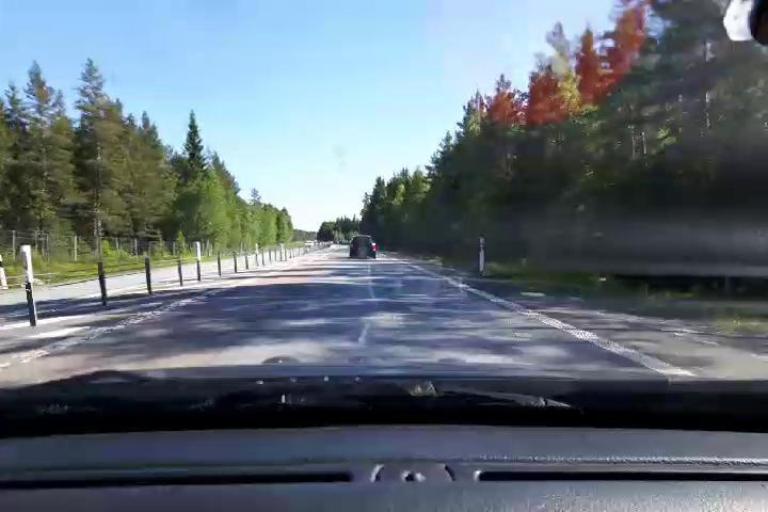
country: SE
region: Gaevleborg
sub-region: Gavle Kommun
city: Norrsundet
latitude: 60.8723
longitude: 17.0507
